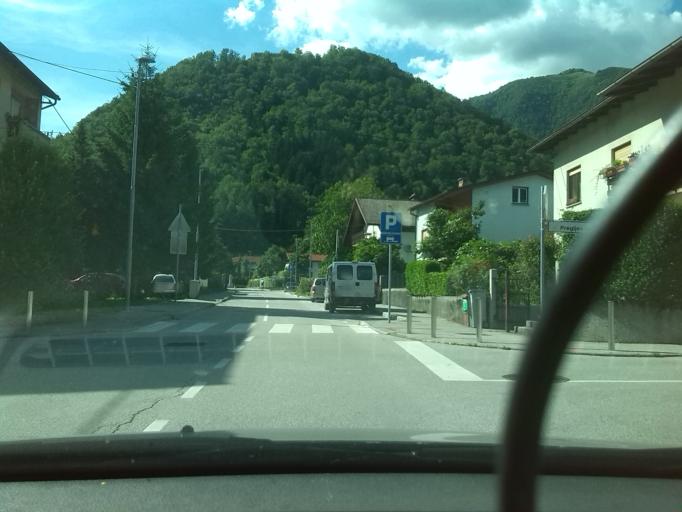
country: SI
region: Tolmin
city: Tolmin
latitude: 46.1853
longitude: 13.7307
